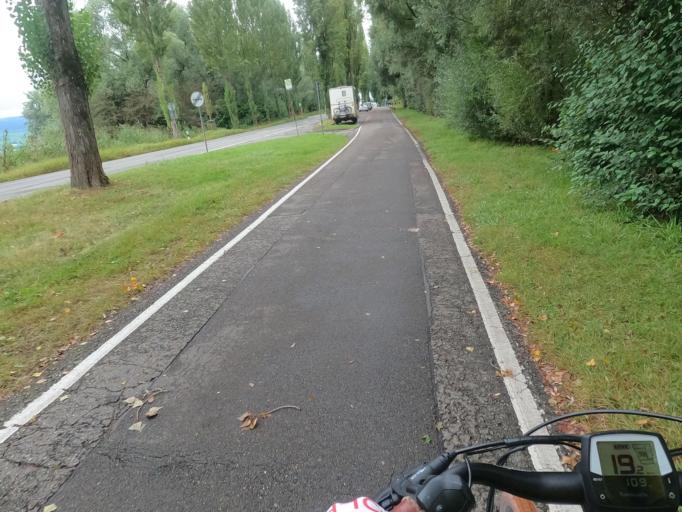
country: CH
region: Thurgau
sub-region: Kreuzlingen District
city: Ermatingen
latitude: 47.6874
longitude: 9.0934
